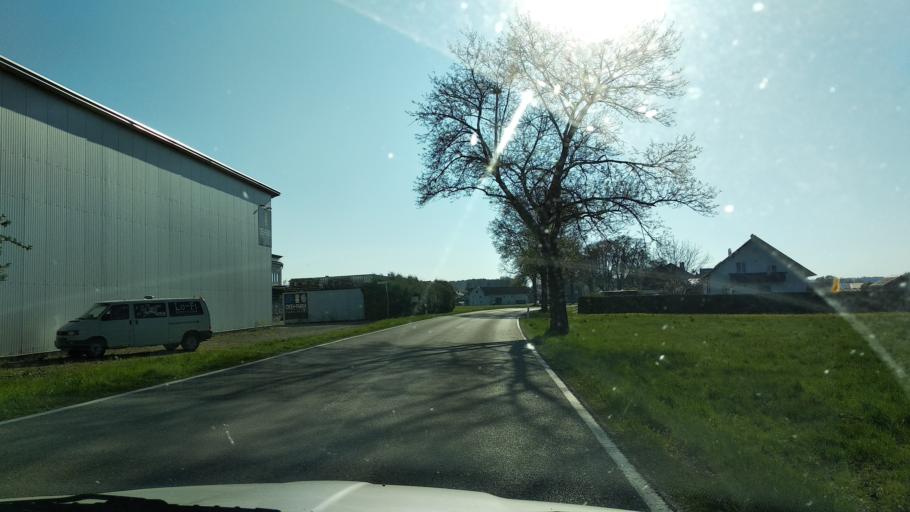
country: DE
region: Bavaria
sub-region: Swabia
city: Westerheim
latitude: 48.0237
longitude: 10.3020
